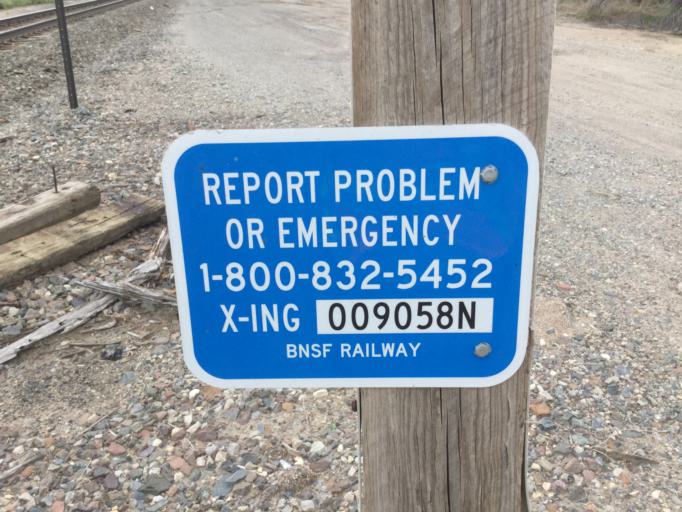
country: US
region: Kansas
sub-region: Edwards County
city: Kinsley
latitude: 37.9275
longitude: -99.4051
